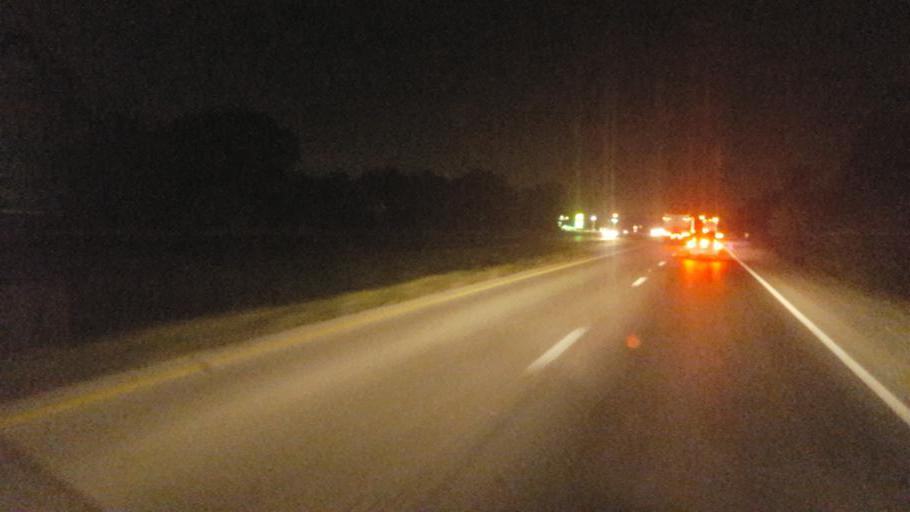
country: US
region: Ohio
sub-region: Franklin County
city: Obetz
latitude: 39.8655
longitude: -83.0047
